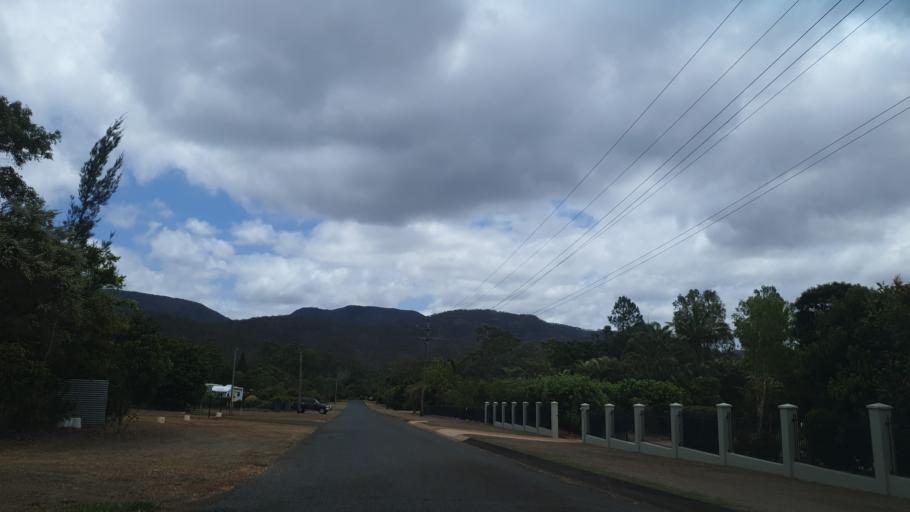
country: AU
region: Queensland
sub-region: Tablelands
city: Tolga
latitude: -17.2075
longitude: 145.4421
